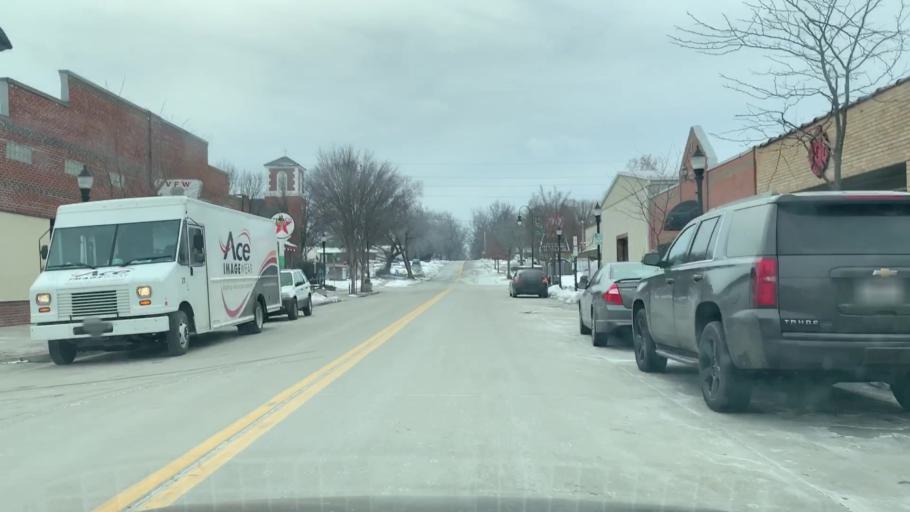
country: US
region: Missouri
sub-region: Jackson County
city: Lees Summit
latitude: 38.9117
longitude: -94.3757
